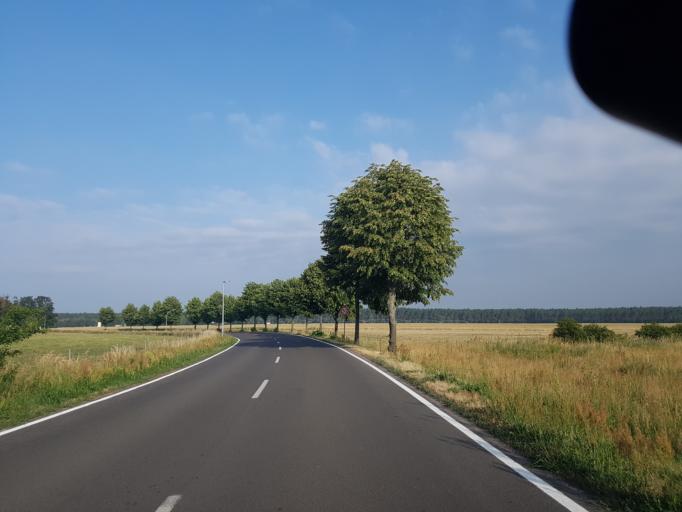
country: DE
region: Saxony-Anhalt
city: Holzdorf
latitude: 51.8553
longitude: 13.0988
